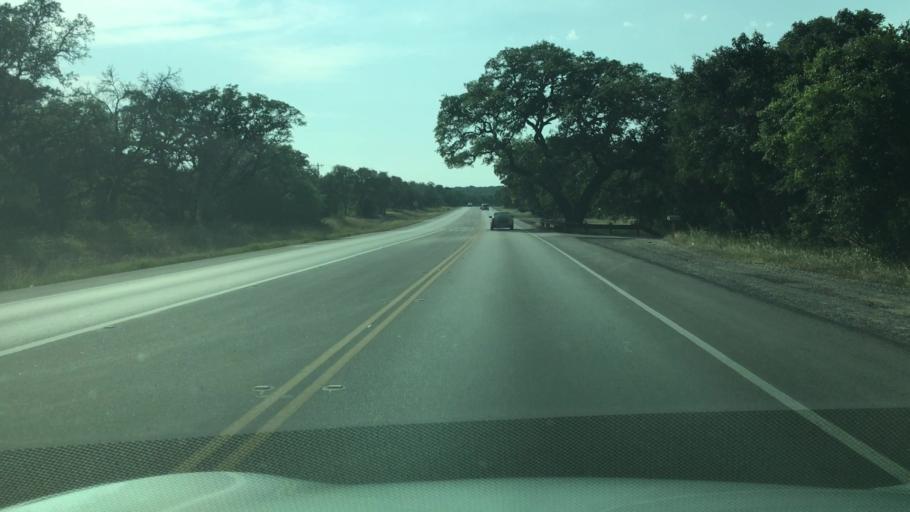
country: US
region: Texas
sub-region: Hays County
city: Wimberley
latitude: 29.9311
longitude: -98.0727
